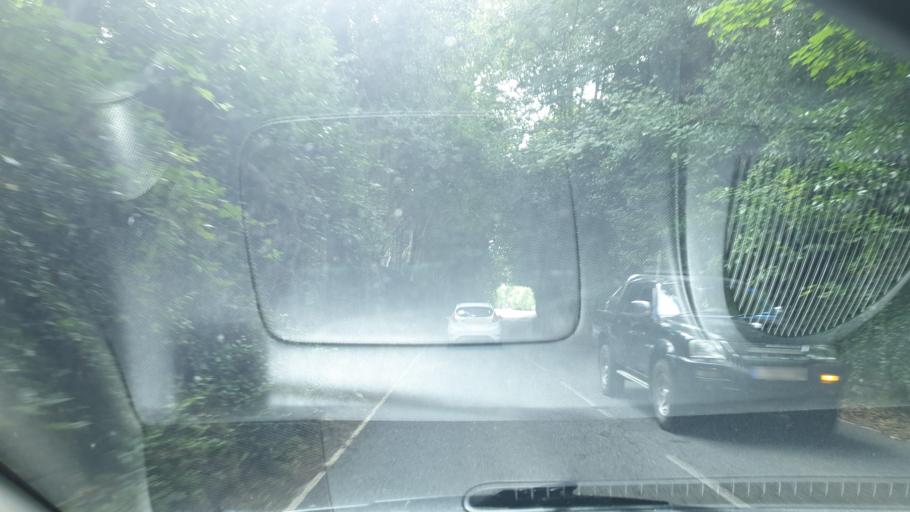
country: GB
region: England
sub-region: West Sussex
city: East Grinstead
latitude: 51.1285
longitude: -0.0038
